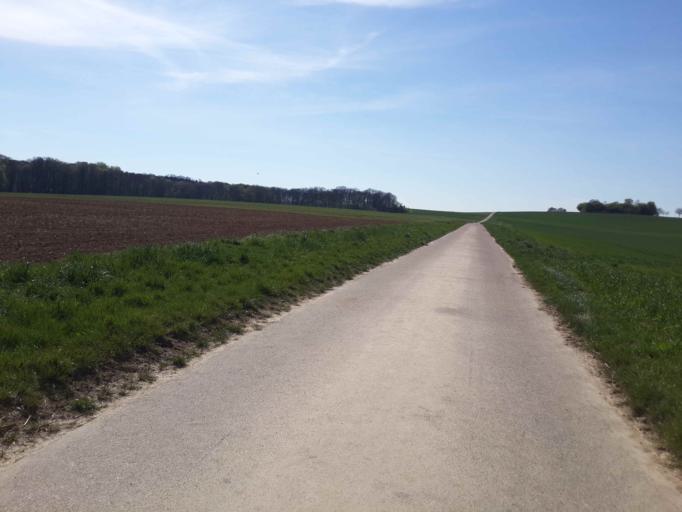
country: DE
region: Baden-Wuerttemberg
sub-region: Regierungsbezirk Stuttgart
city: Leingarten
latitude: 49.1814
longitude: 9.0947
